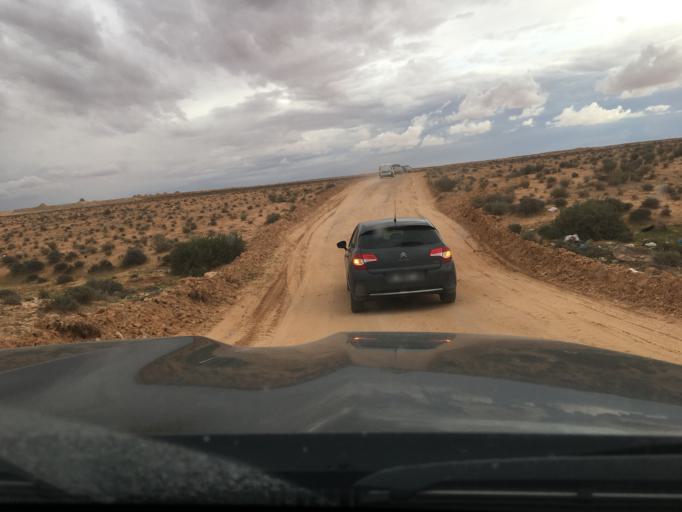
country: TN
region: Madanin
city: Medenine
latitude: 33.2636
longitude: 10.5712
